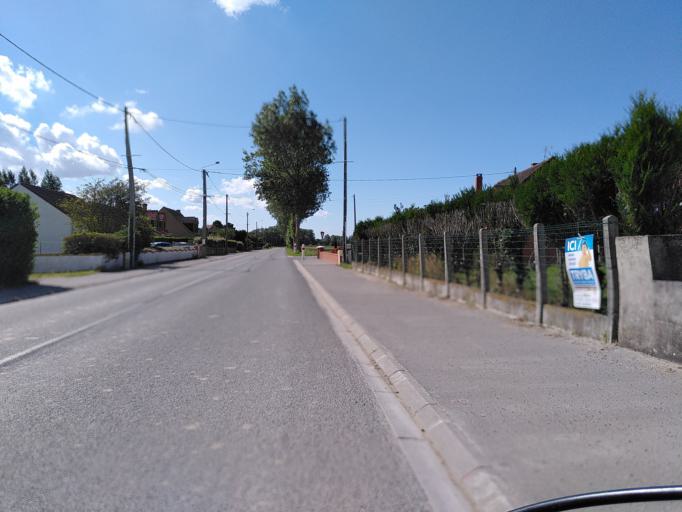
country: FR
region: Nord-Pas-de-Calais
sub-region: Departement du Nord
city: Grand-Fort-Philippe
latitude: 50.9883
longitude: 2.0774
